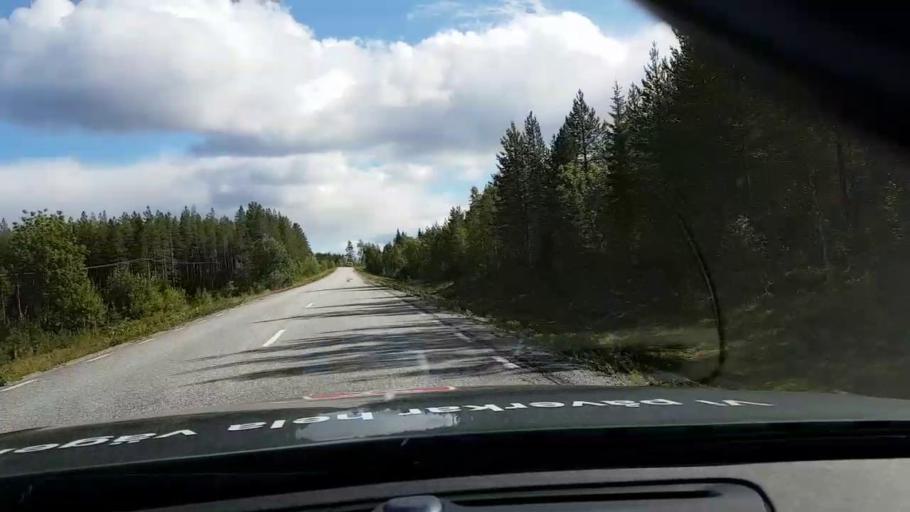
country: SE
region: Vaesterbotten
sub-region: Asele Kommun
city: Asele
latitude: 63.7749
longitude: 17.6740
